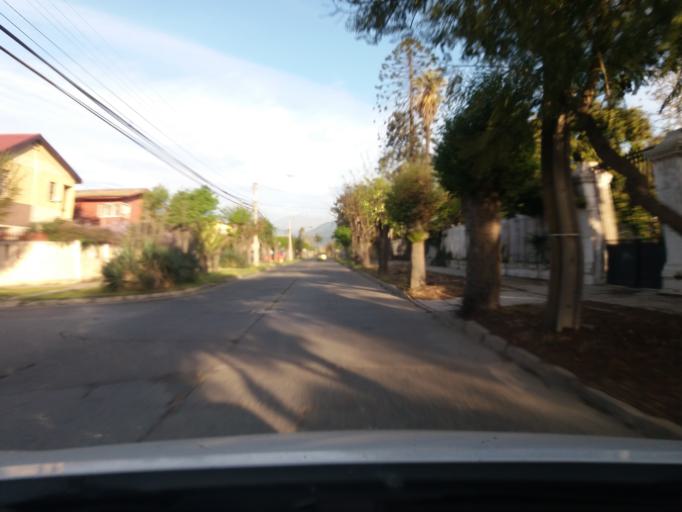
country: CL
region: Valparaiso
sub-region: Provincia de Marga Marga
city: Limache
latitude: -32.9912
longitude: -71.2692
